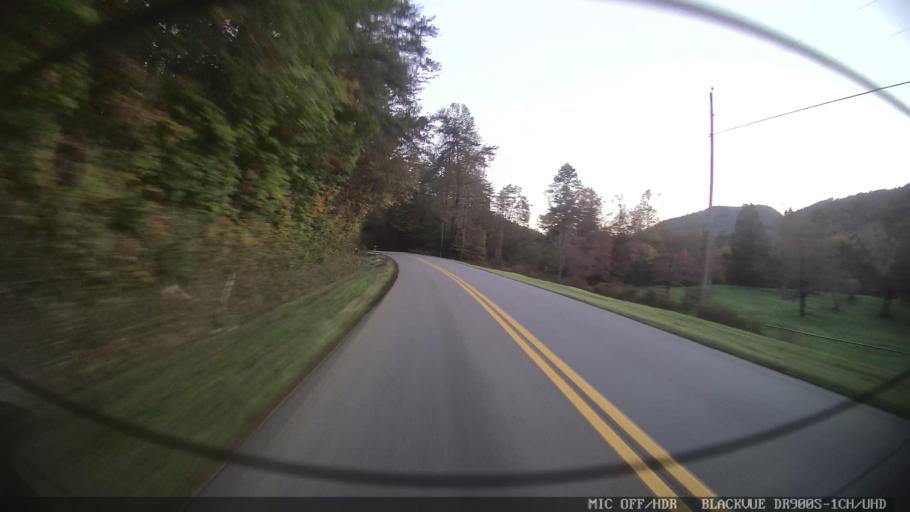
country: US
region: Georgia
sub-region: Union County
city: Blairsville
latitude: 34.8958
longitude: -83.8688
